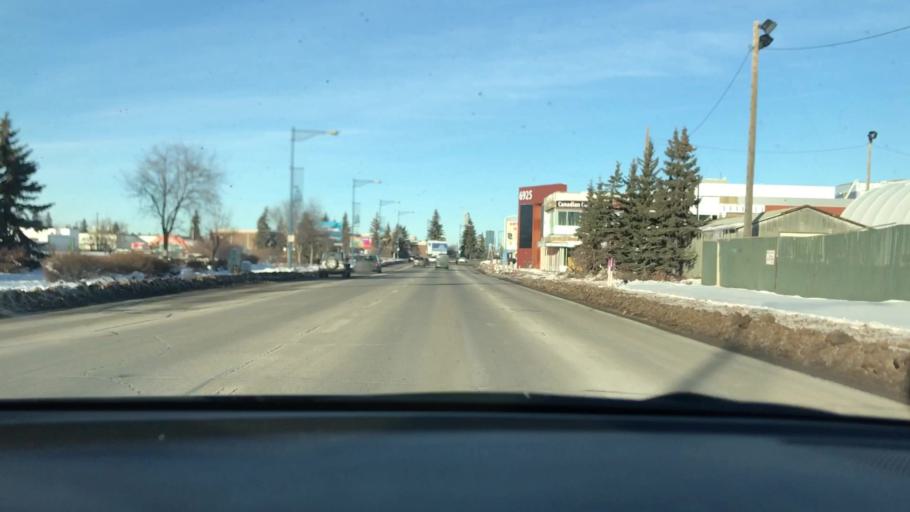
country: CA
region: Alberta
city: Edmonton
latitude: 53.5051
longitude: -113.4947
